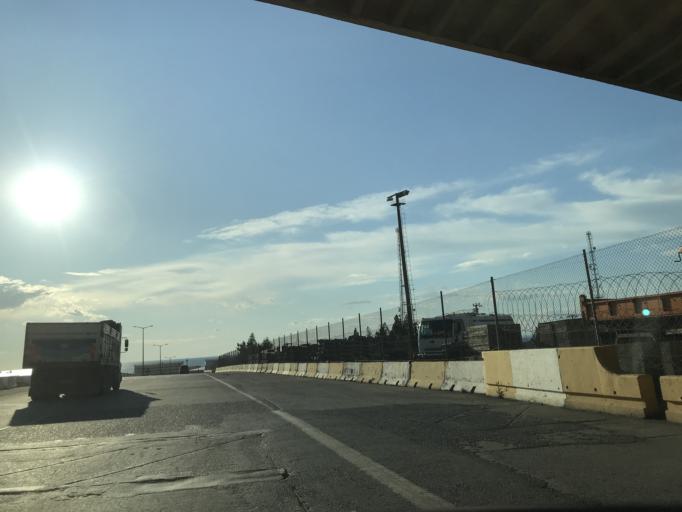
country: TR
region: Hatay
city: Guzelkoy
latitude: 36.6078
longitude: 36.2044
